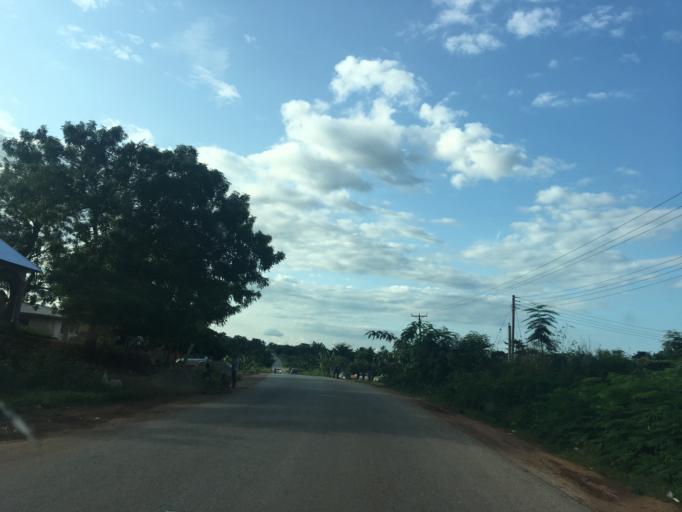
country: GH
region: Western
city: Bibiani
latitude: 6.3063
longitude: -2.2505
